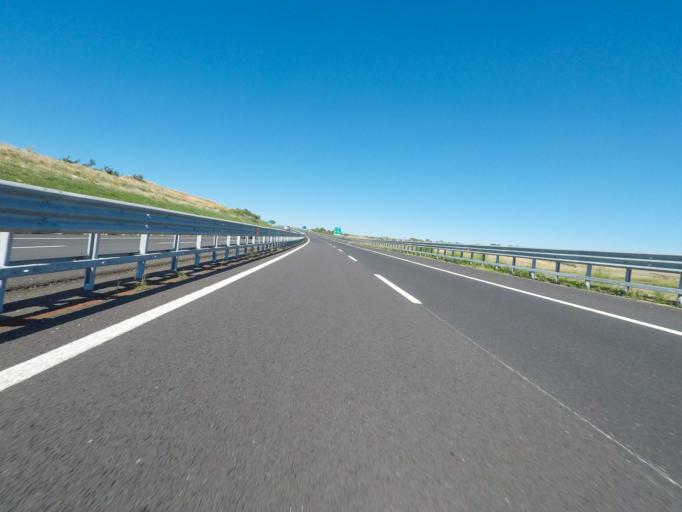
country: IT
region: Latium
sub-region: Provincia di Viterbo
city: Tarquinia
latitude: 42.2026
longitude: 11.7852
